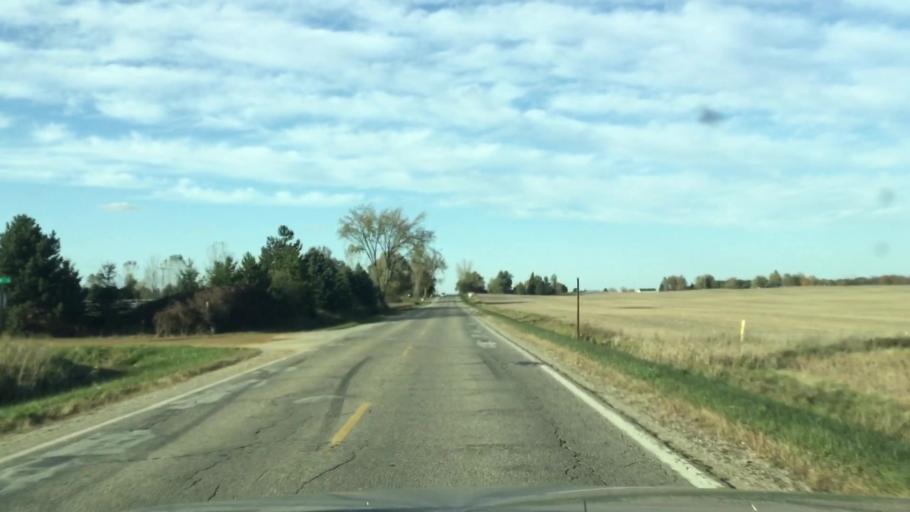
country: US
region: Michigan
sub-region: Lapeer County
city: North Branch
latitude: 43.2597
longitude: -83.1978
